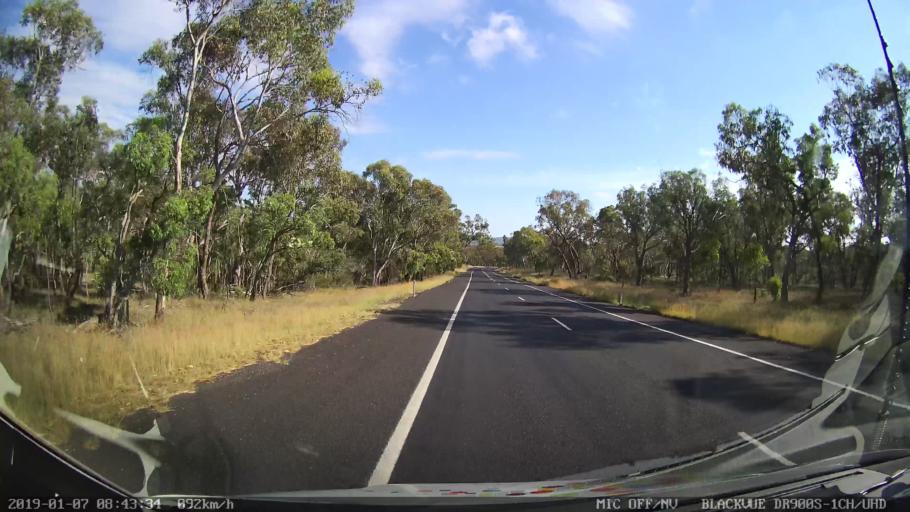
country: AU
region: New South Wales
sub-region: Tamworth Municipality
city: Kootingal
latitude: -30.8431
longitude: 151.2153
